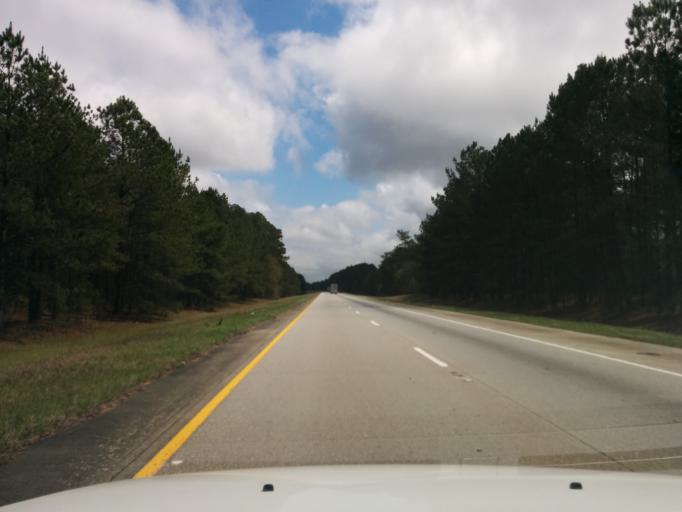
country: US
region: Georgia
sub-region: Emanuel County
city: Swainsboro
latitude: 32.4094
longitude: -82.3574
